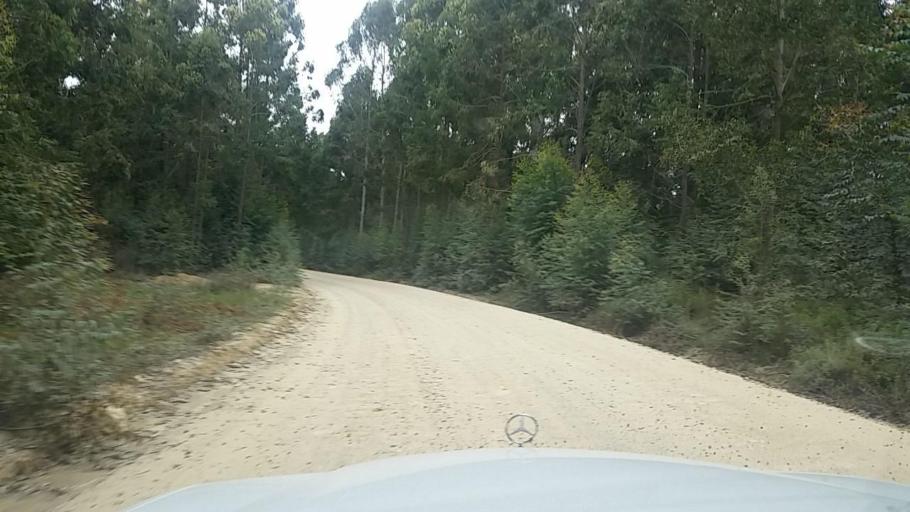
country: ZA
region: Western Cape
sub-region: Eden District Municipality
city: Knysna
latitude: -33.9784
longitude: 23.1367
